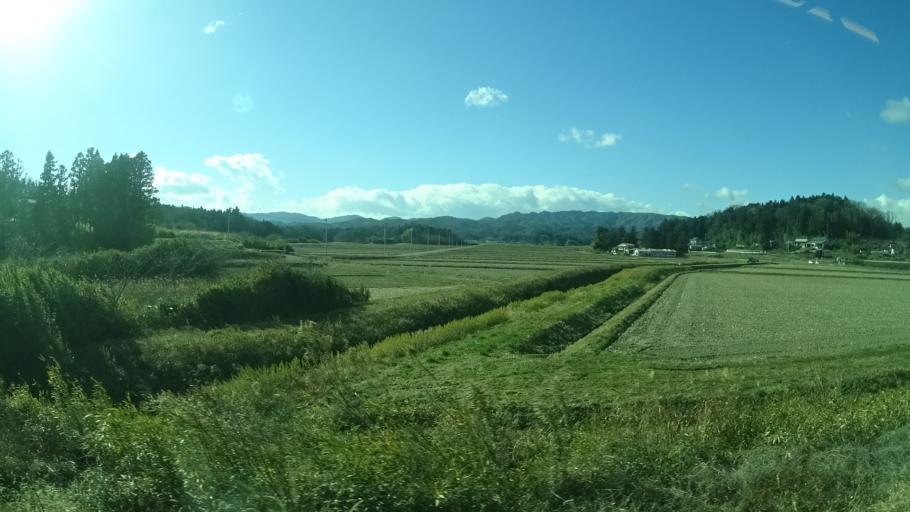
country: JP
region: Miyagi
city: Marumori
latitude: 37.7586
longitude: 140.9325
